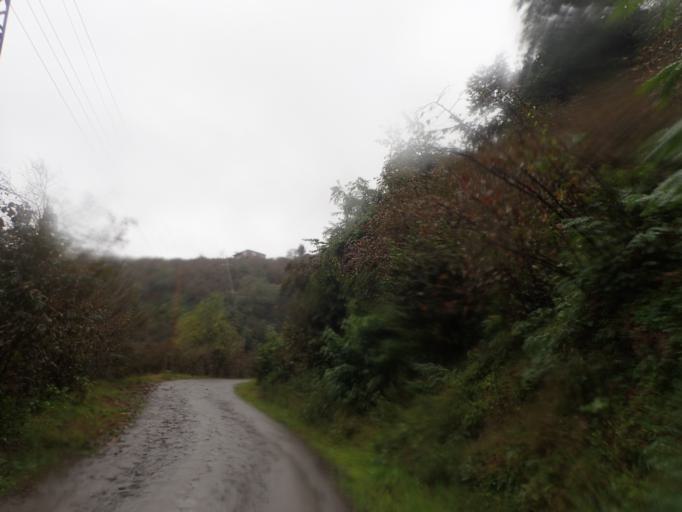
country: TR
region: Ordu
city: Persembe
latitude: 41.0345
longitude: 37.7248
